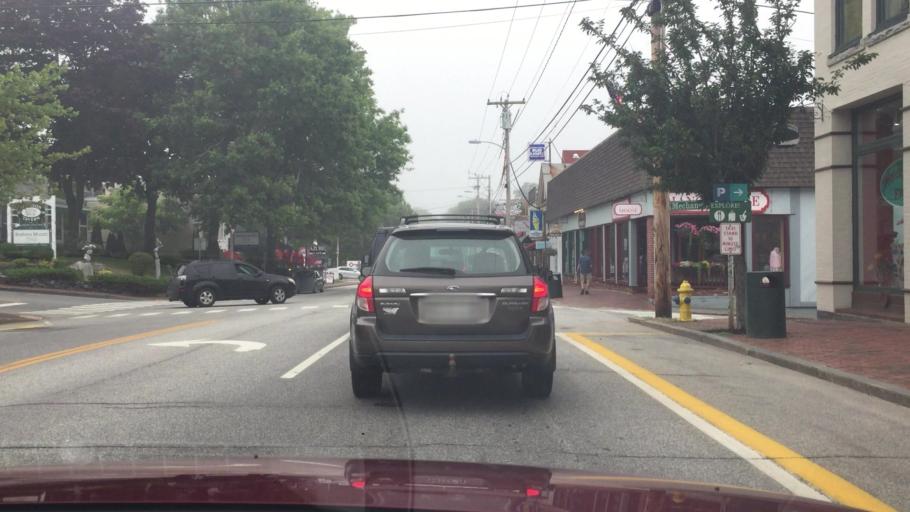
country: US
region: Maine
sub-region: Cumberland County
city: Freeport
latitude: 43.8577
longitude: -70.1026
